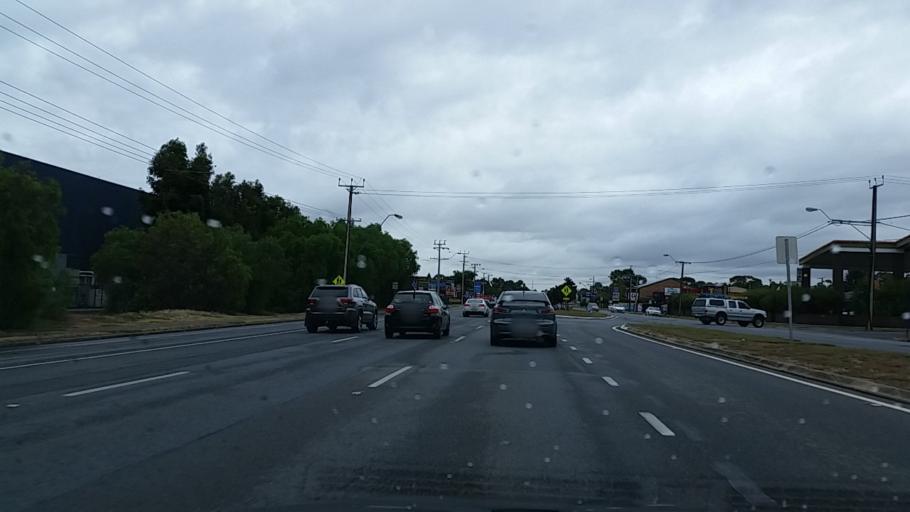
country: AU
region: South Australia
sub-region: Salisbury
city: Ingle Farm
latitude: -34.8289
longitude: 138.6140
